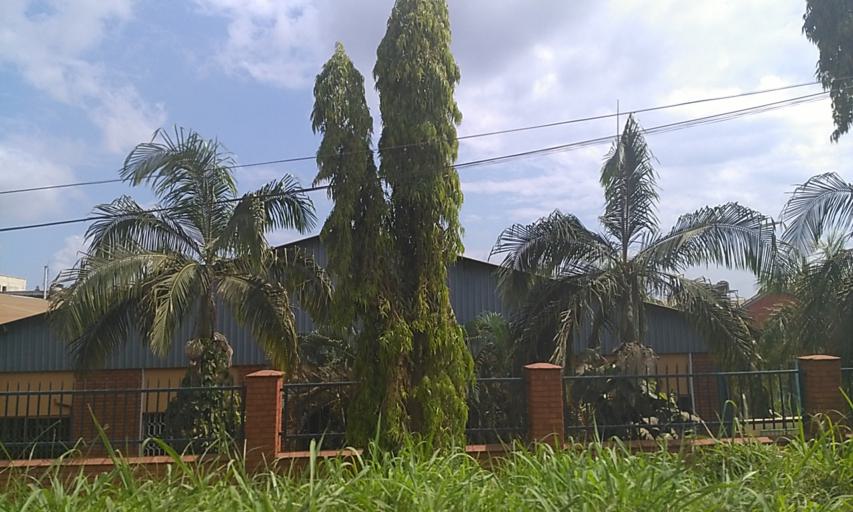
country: UG
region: Central Region
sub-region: Wakiso District
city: Kireka
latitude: 0.3405
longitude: 32.6169
